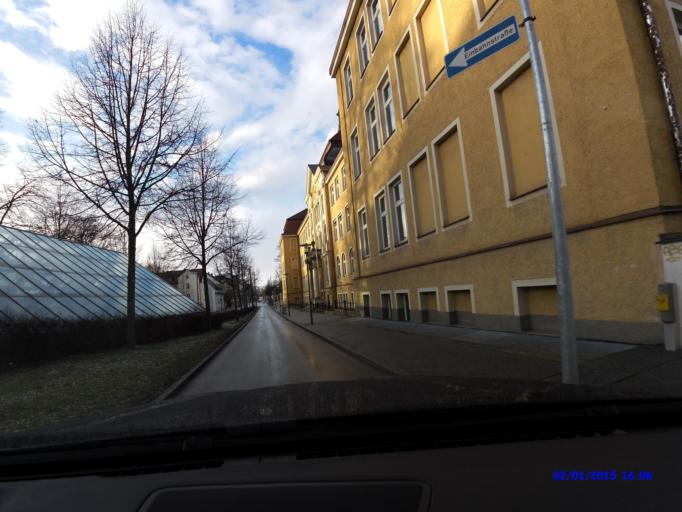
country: DE
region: Bavaria
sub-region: Lower Bavaria
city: Landshut
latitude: 48.5371
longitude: 12.1614
